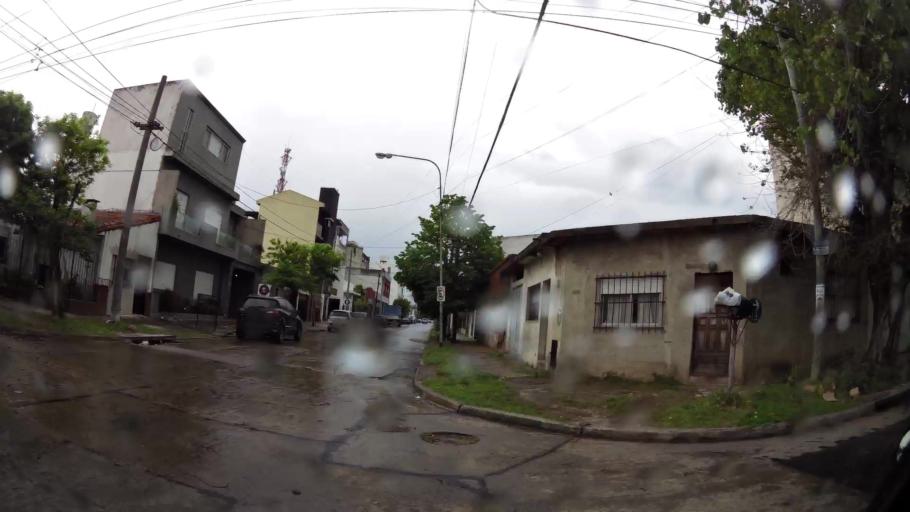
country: AR
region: Buenos Aires
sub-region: Partido de Quilmes
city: Quilmes
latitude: -34.7645
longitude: -58.2175
